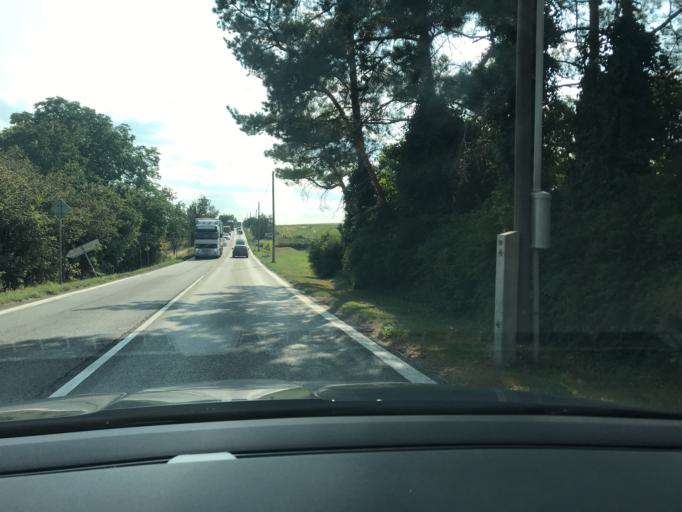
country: CZ
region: Central Bohemia
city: Brandysek
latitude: 50.2541
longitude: 14.1602
